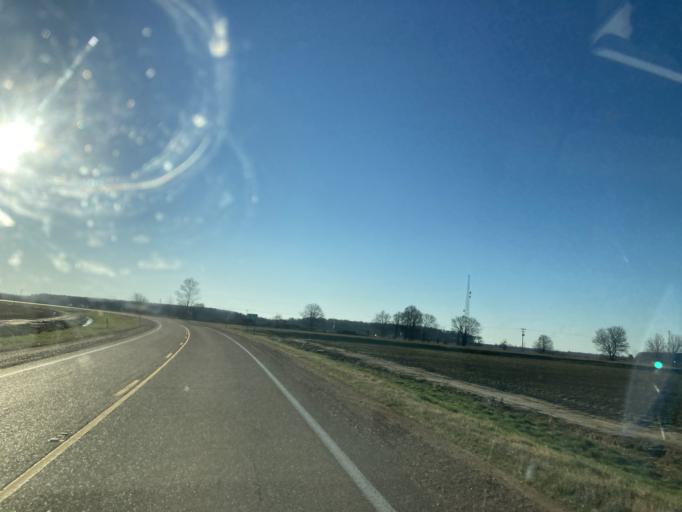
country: US
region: Mississippi
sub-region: Yazoo County
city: Yazoo City
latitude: 32.9302
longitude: -90.5858
